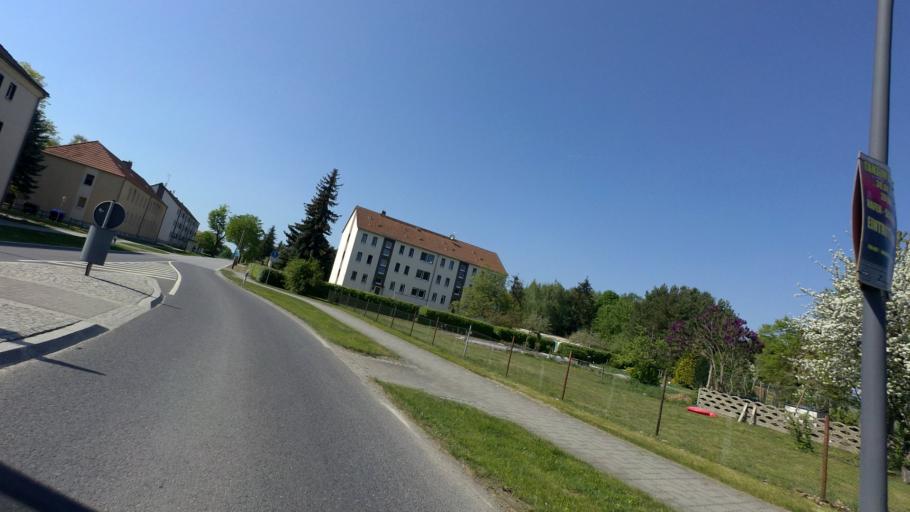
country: DE
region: Brandenburg
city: Schlepzig
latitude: 52.0434
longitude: 14.0259
